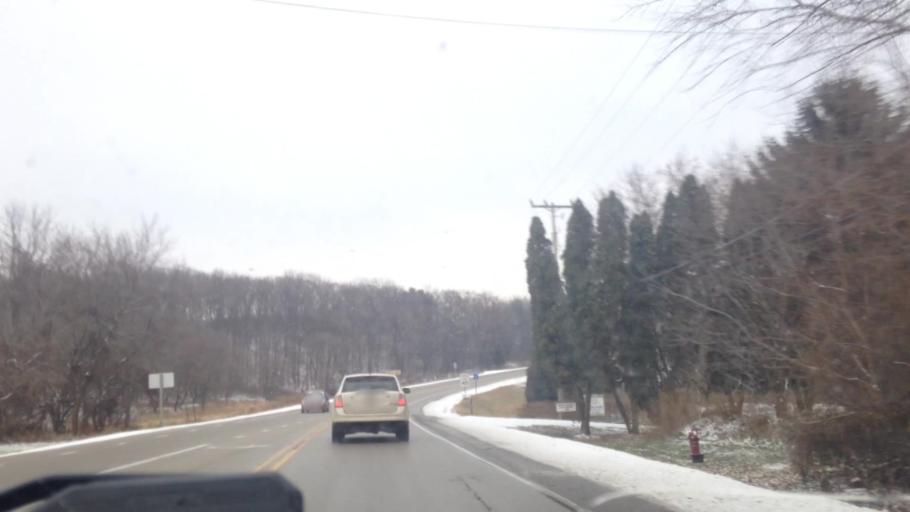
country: US
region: Wisconsin
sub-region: Waukesha County
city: Hartland
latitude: 43.0759
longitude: -88.3636
